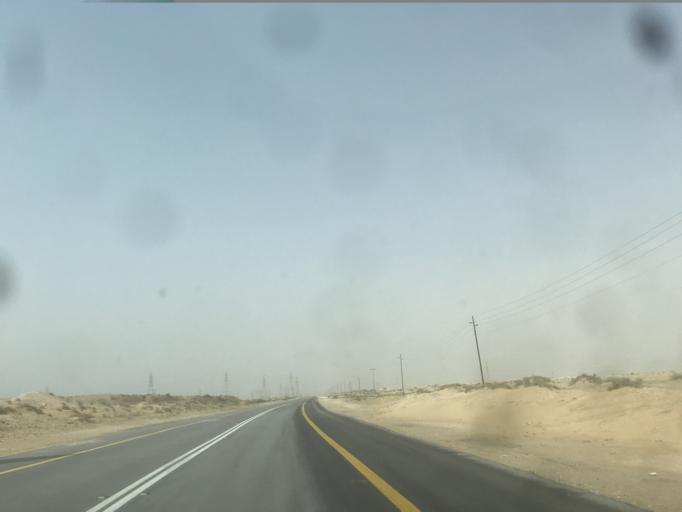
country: SA
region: Eastern Province
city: Abqaiq
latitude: 25.9348
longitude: 49.7297
